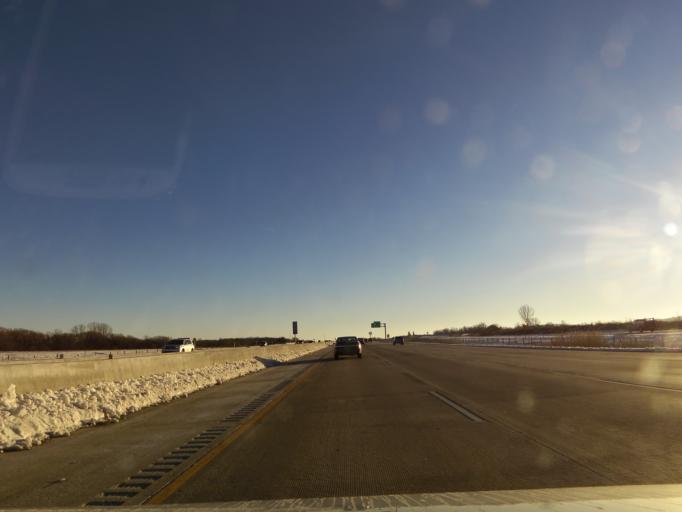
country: US
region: Wisconsin
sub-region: Kenosha County
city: Pleasant Prairie
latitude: 42.5970
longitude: -87.9524
